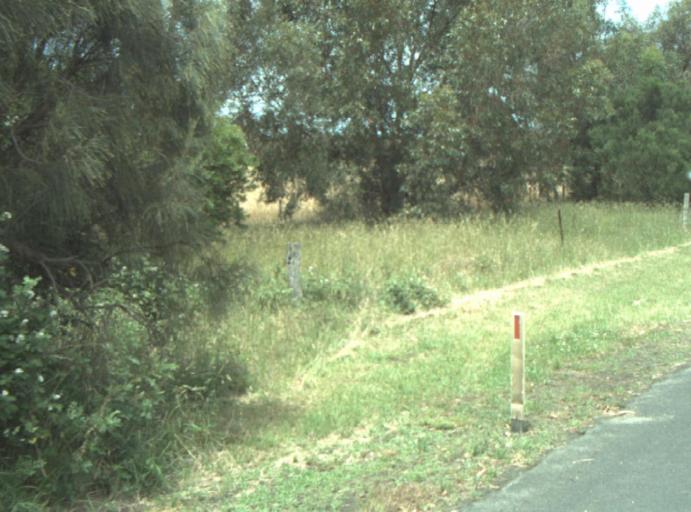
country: AU
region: Victoria
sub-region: Greater Geelong
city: Wandana Heights
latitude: -38.2316
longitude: 144.2798
